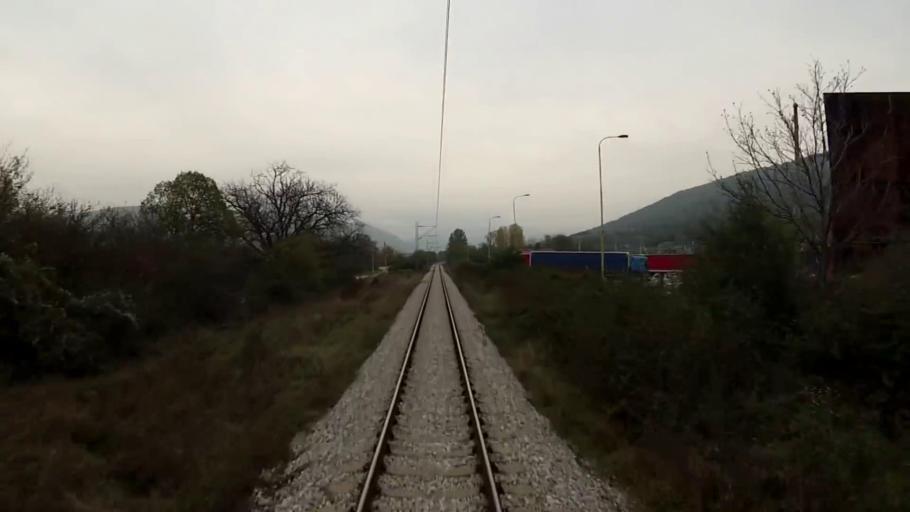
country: RS
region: Central Serbia
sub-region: Pirotski Okrug
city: Dimitrovgrad
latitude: 43.0029
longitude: 22.8192
